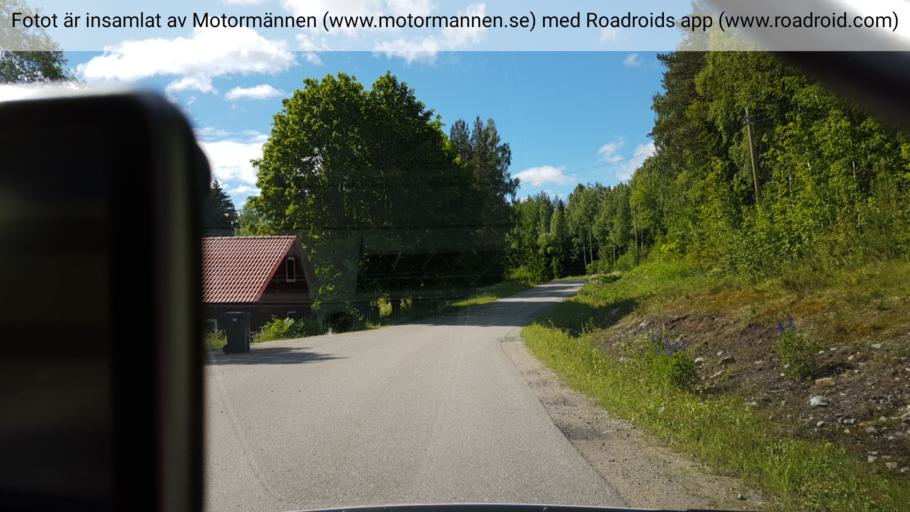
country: SE
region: Gaevleborg
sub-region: Hudiksvalls Kommun
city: Sorforsa
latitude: 61.6897
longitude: 16.9219
